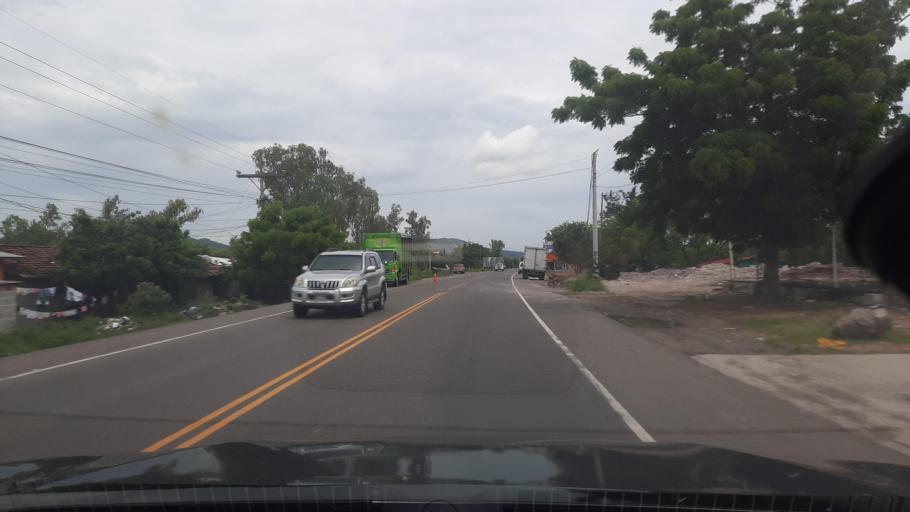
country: HN
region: Valle
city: Jicaro Galan
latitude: 13.5264
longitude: -87.4385
